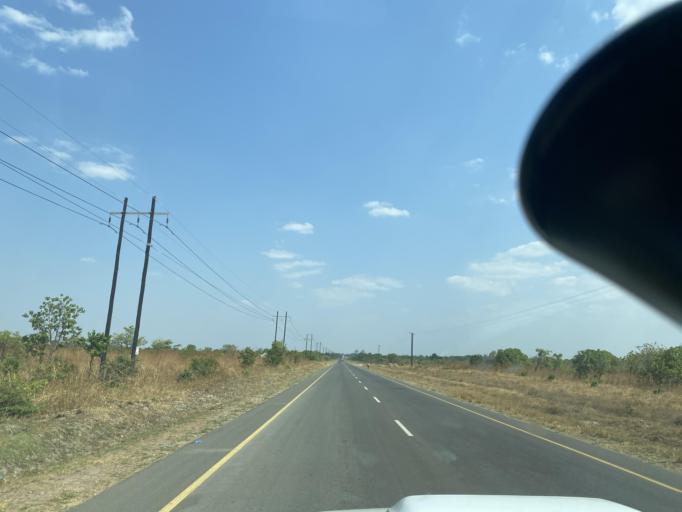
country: ZM
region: Lusaka
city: Lusaka
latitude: -15.3229
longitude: 28.0647
